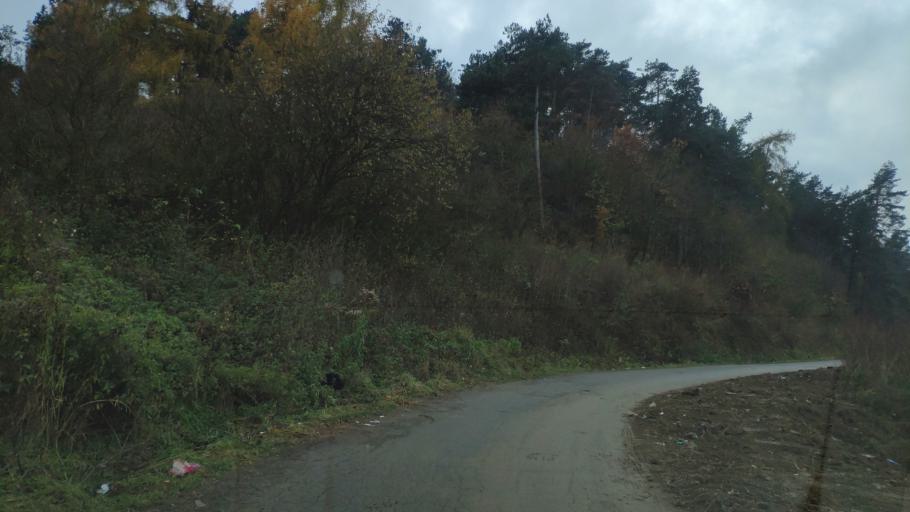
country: SK
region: Presovsky
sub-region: Okres Presov
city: Presov
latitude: 49.0315
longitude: 21.2035
